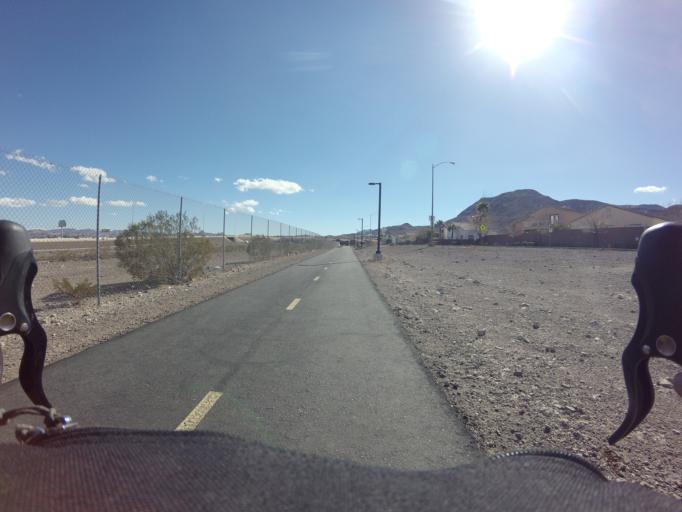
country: US
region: Nevada
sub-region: Clark County
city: Henderson
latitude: 36.0302
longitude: -115.0139
